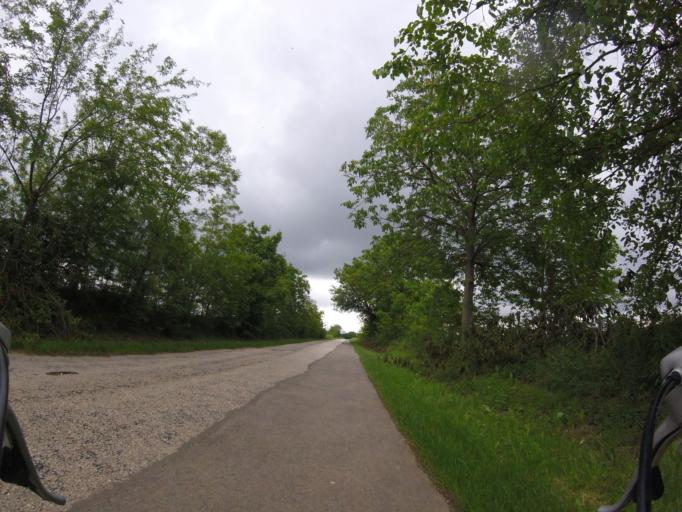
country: HU
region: Baranya
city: Pellerd
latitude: 45.9690
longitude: 18.1460
